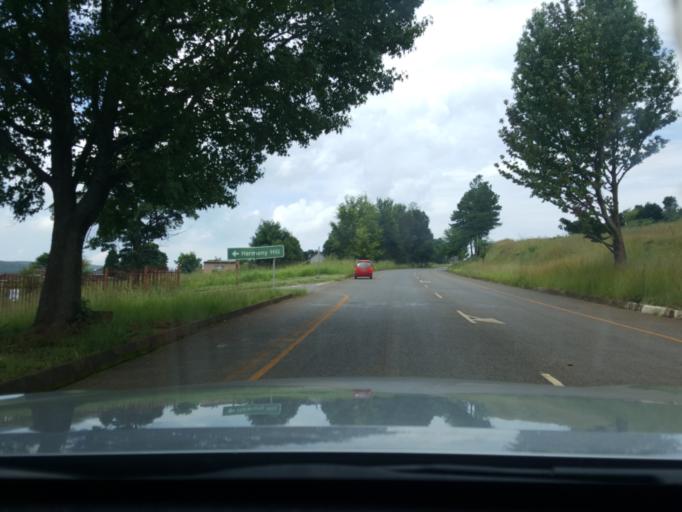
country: ZA
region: Mpumalanga
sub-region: Ehlanzeni District
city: Graksop
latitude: -25.1014
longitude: 30.7880
